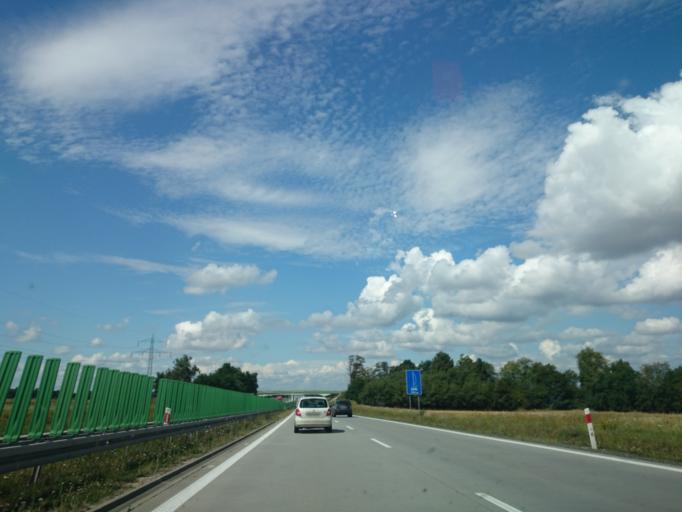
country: PL
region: Lower Silesian Voivodeship
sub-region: Powiat legnicki
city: Legnickie Pole
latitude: 51.1482
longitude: 16.2598
